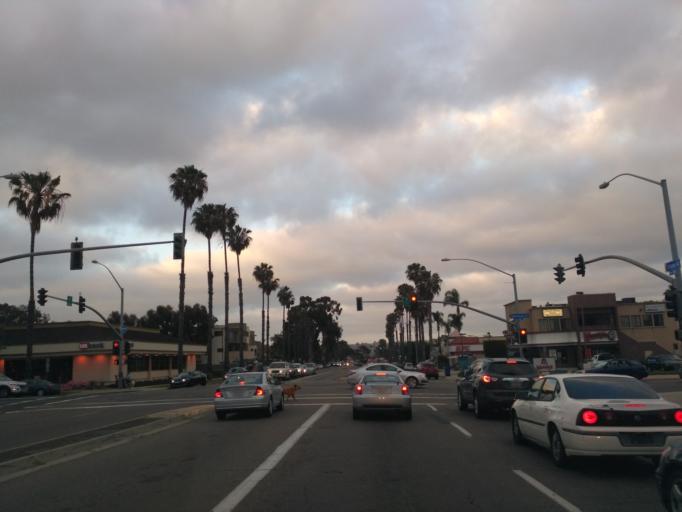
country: US
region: California
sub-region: San Diego County
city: La Jolla
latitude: 32.7977
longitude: -117.2408
